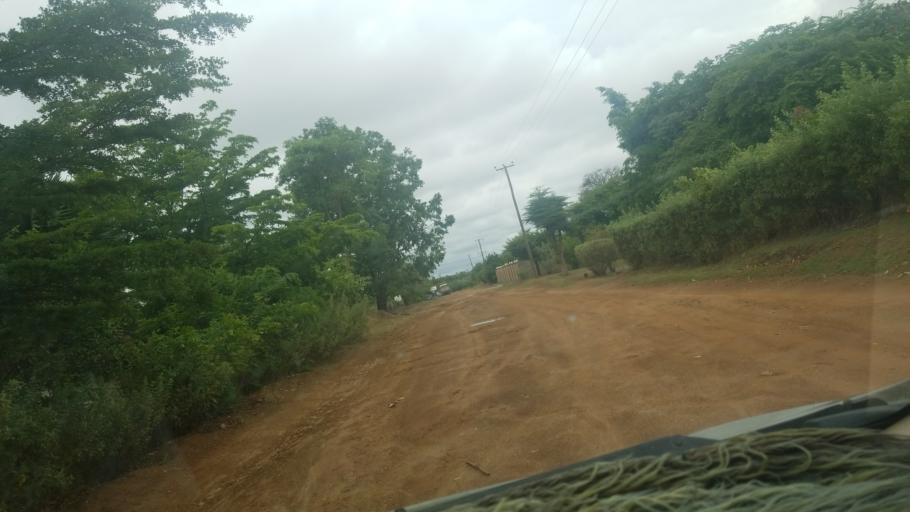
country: ZM
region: Luapula
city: Mansa
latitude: -11.1951
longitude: 28.8995
